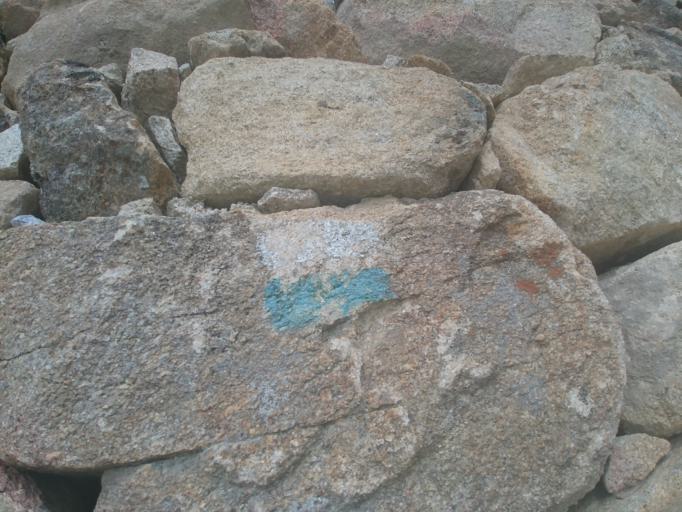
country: ES
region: Extremadura
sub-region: Provincia de Caceres
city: Casas del Castanar
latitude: 40.1346
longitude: -5.9480
